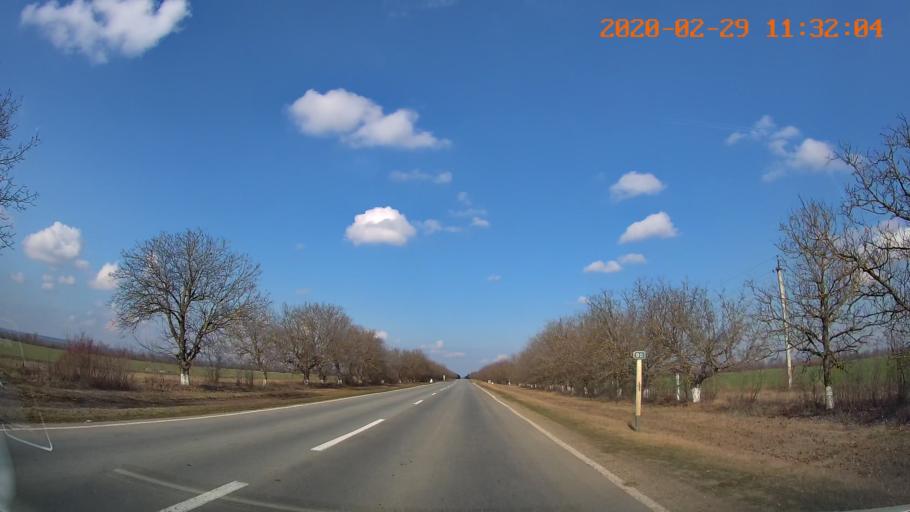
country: MD
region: Rezina
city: Saharna
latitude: 47.5326
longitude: 29.0983
